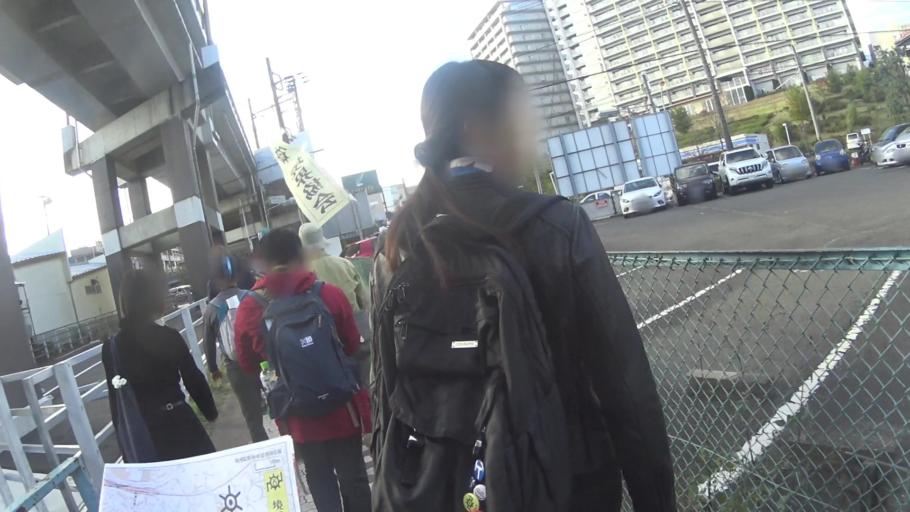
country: JP
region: Tokyo
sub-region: Machida-shi
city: Machida
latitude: 35.6191
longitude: 139.4749
